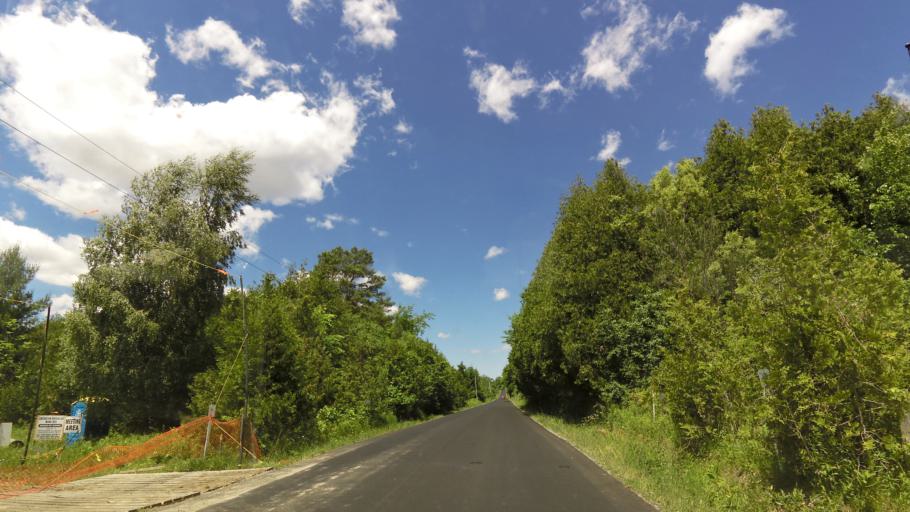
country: CA
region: Ontario
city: Oshawa
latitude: 43.9587
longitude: -78.5823
